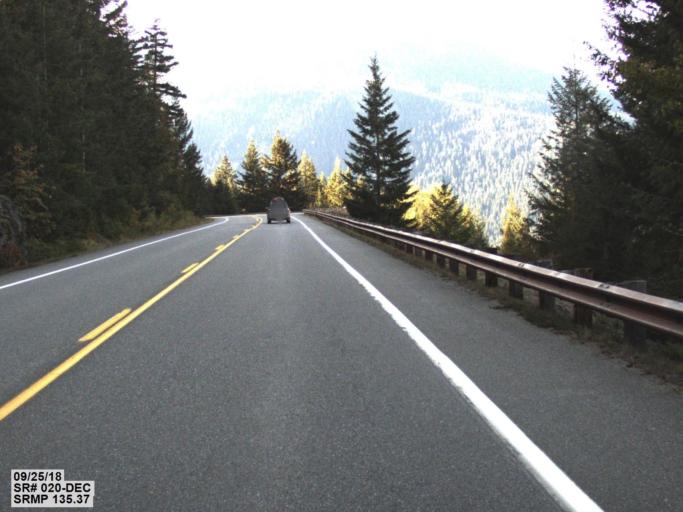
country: US
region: Washington
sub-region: Snohomish County
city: Darrington
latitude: 48.7266
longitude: -121.0356
